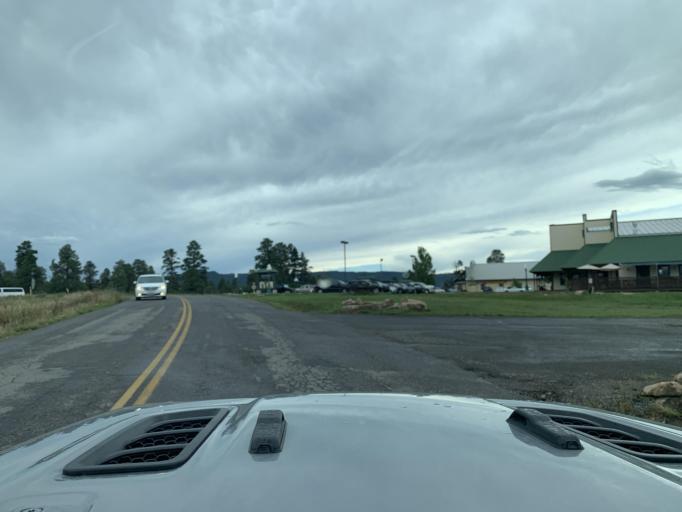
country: US
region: Colorado
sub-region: Archuleta County
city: Pagosa Springs
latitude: 37.2543
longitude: -107.0794
